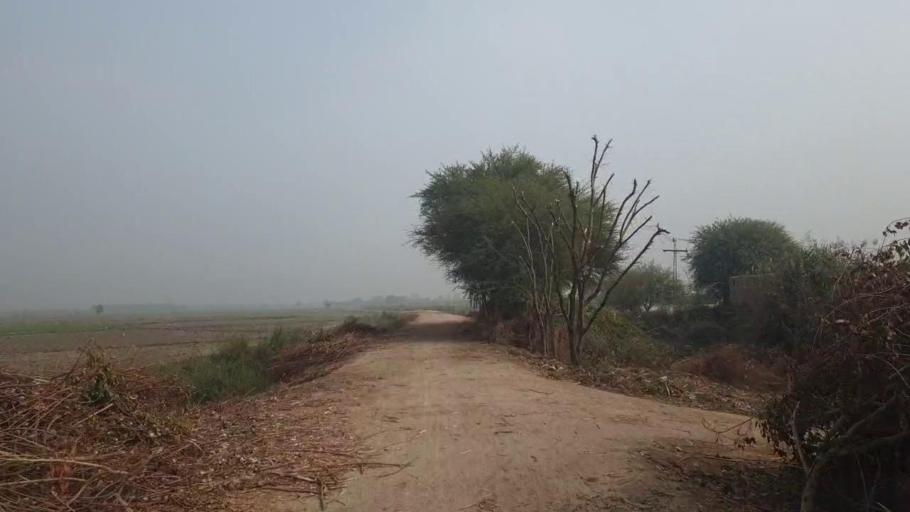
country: PK
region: Sindh
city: Tando Adam
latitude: 25.7587
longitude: 68.6153
